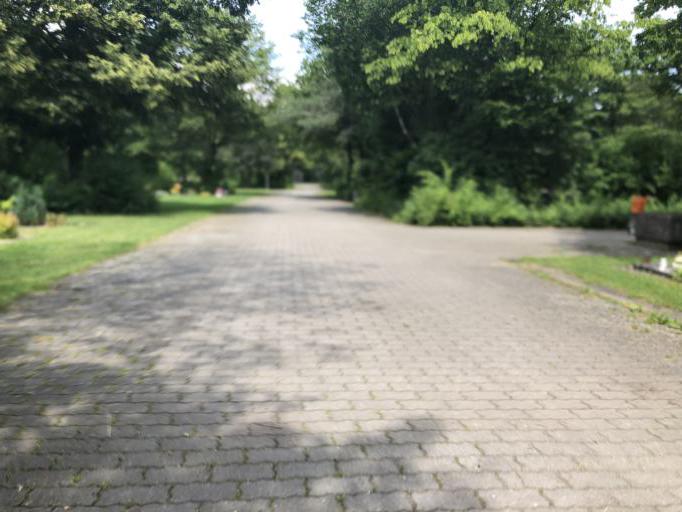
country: DE
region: Bavaria
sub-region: Regierungsbezirk Mittelfranken
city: Obermichelbach
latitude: 49.5745
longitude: 10.9438
